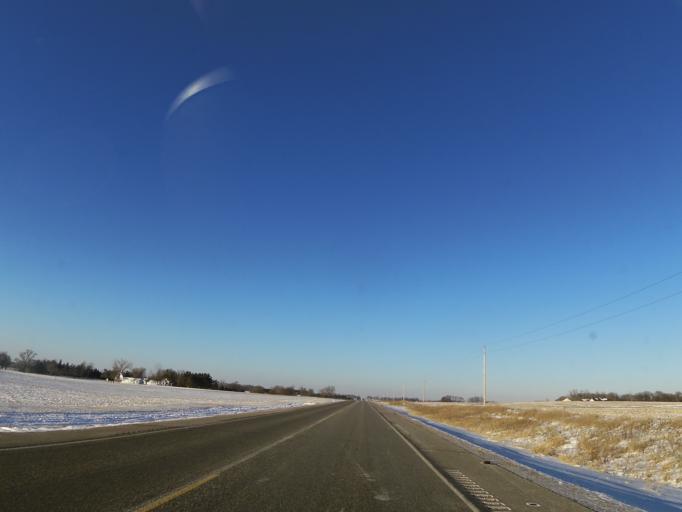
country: US
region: Minnesota
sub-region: Rice County
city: Lonsdale
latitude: 44.4947
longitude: -93.4429
